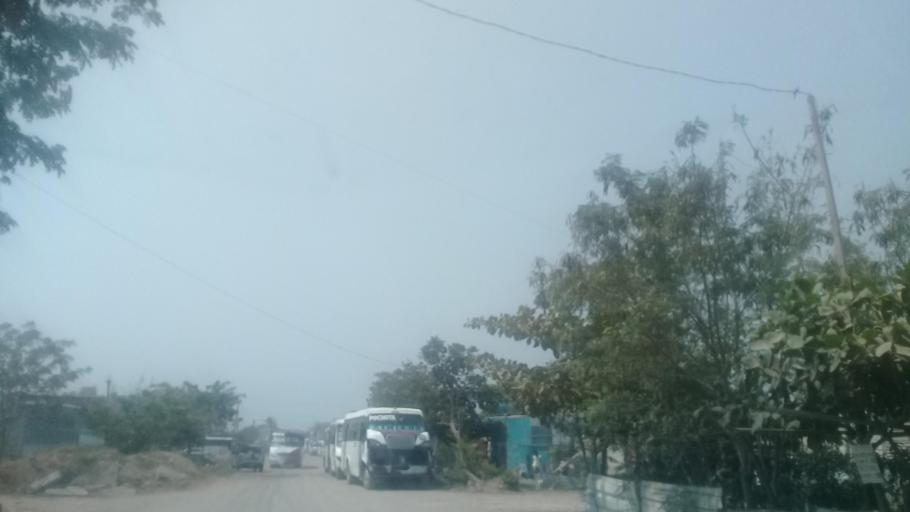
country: MX
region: Veracruz
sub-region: Veracruz
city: Las Amapolas
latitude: 19.1682
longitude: -96.1779
